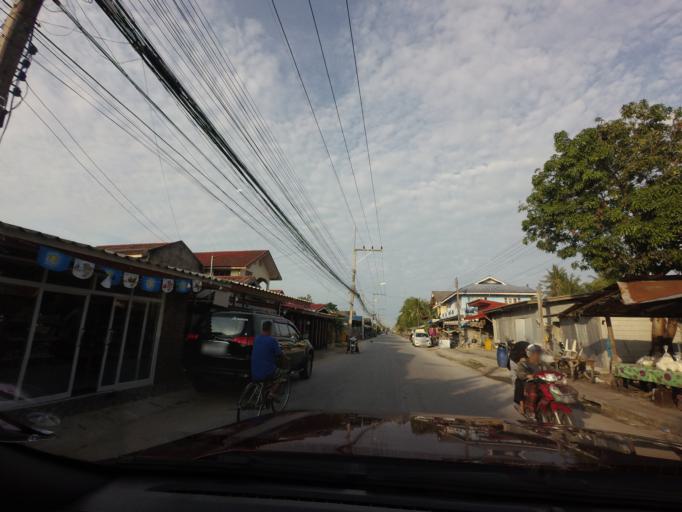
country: TH
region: Pattani
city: Yaring
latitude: 6.8694
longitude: 101.3436
